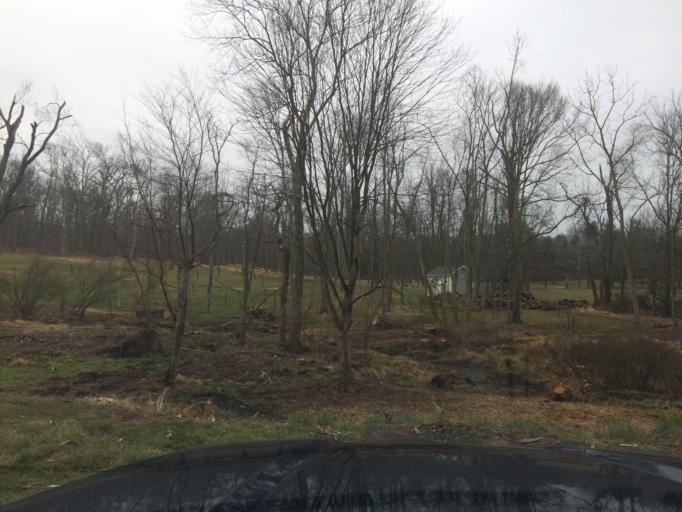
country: US
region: Maryland
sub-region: Carroll County
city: Sykesville
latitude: 39.2954
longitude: -77.0030
